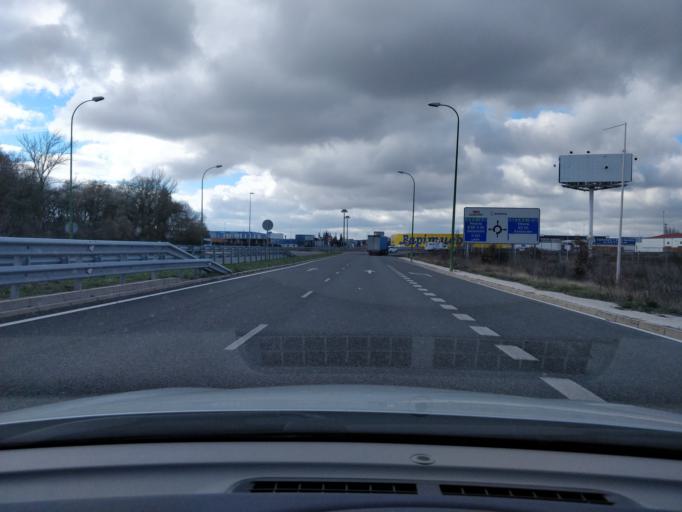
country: ES
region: Castille and Leon
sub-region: Provincia de Burgos
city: Cardenajimeno
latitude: 42.3615
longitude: -3.6374
